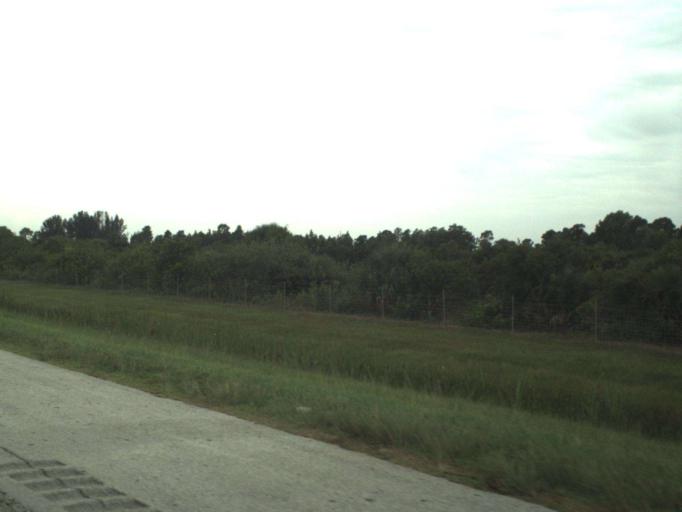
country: US
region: Florida
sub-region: Martin County
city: Hobe Sound
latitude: 27.0341
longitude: -80.2331
